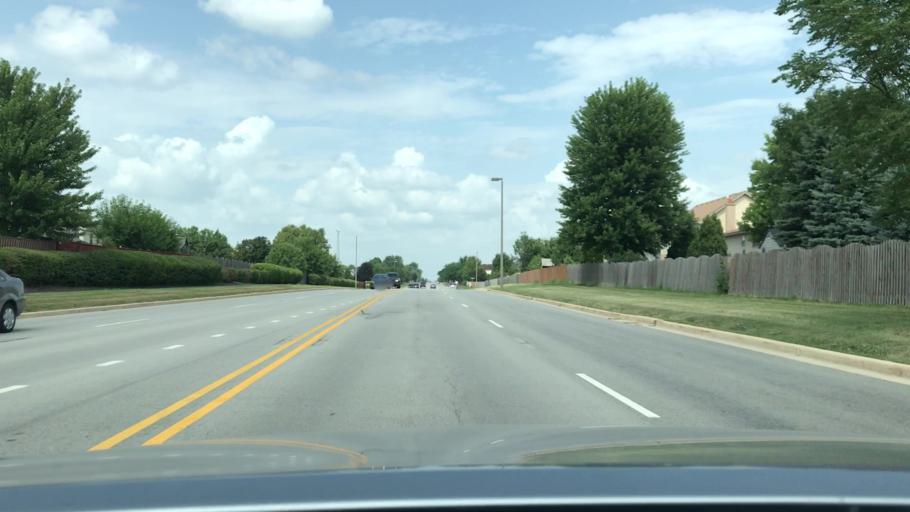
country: US
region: Illinois
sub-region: DuPage County
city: Woodridge
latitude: 41.7376
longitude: -88.0306
